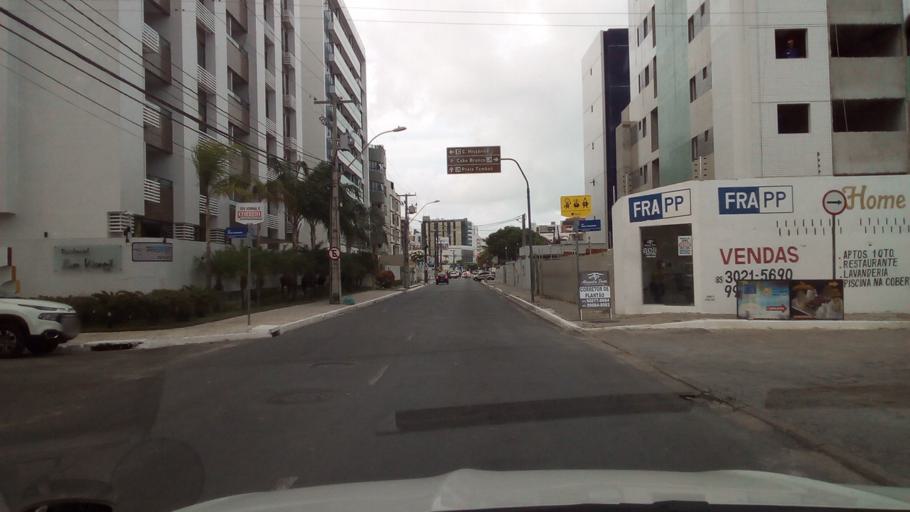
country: BR
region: Paraiba
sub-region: Joao Pessoa
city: Joao Pessoa
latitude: -7.1267
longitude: -34.8258
